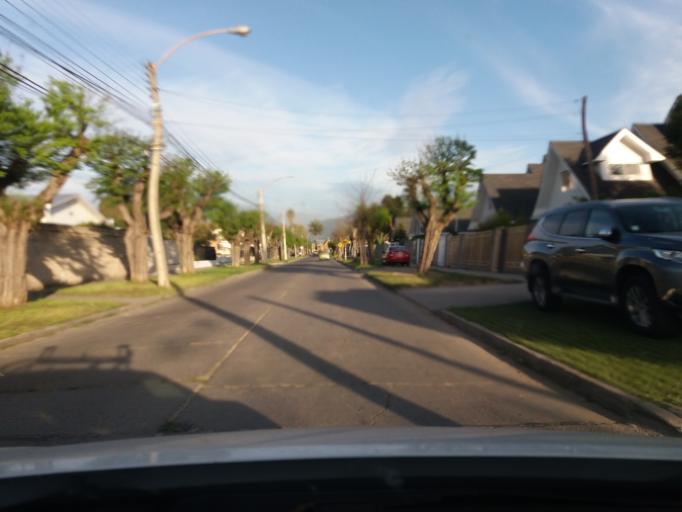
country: CL
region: Valparaiso
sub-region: Provincia de Marga Marga
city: Limache
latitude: -32.9918
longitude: -71.2677
